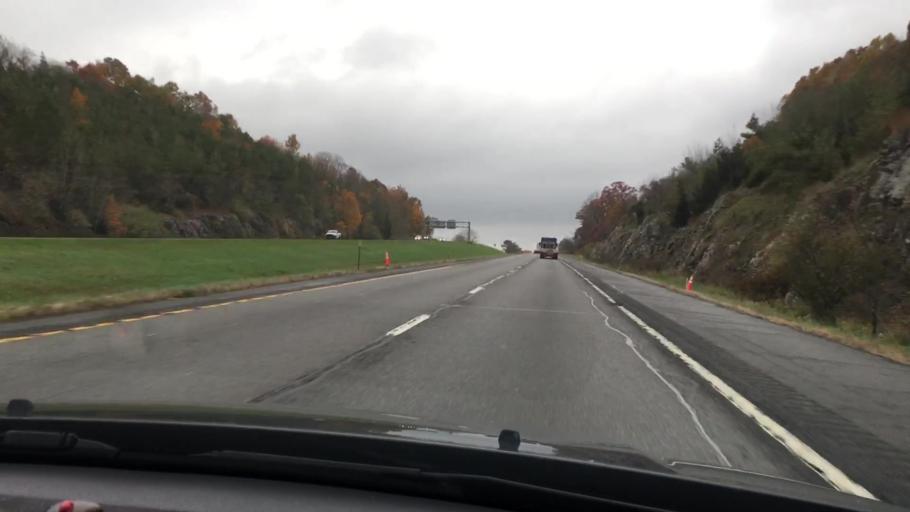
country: US
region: New York
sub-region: Putnam County
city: Brewster
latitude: 41.4033
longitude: -73.6045
